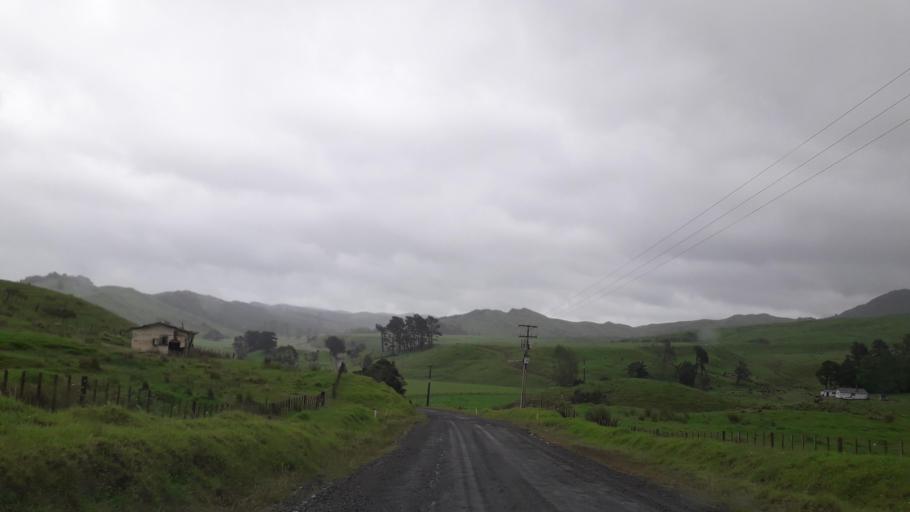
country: NZ
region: Northland
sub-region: Far North District
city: Kaitaia
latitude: -35.4146
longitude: 173.3658
